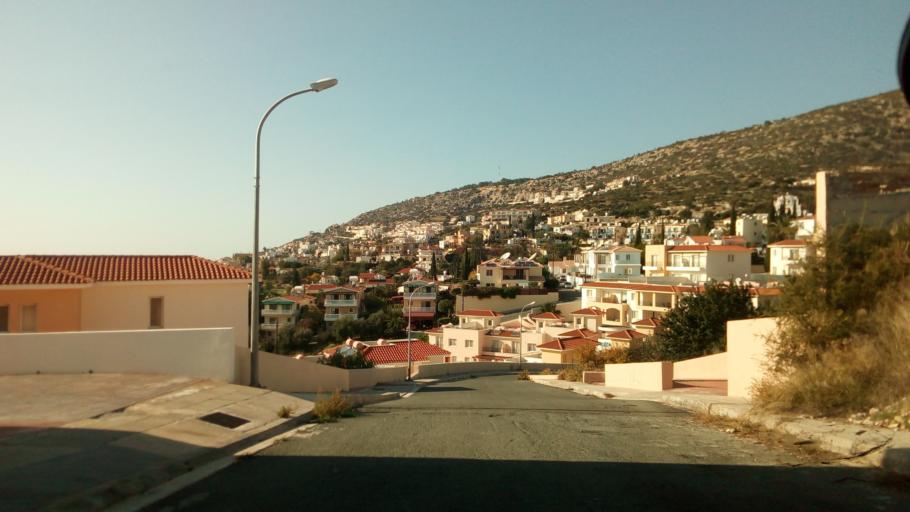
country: CY
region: Pafos
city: Pegeia
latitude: 34.8845
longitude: 32.3884
